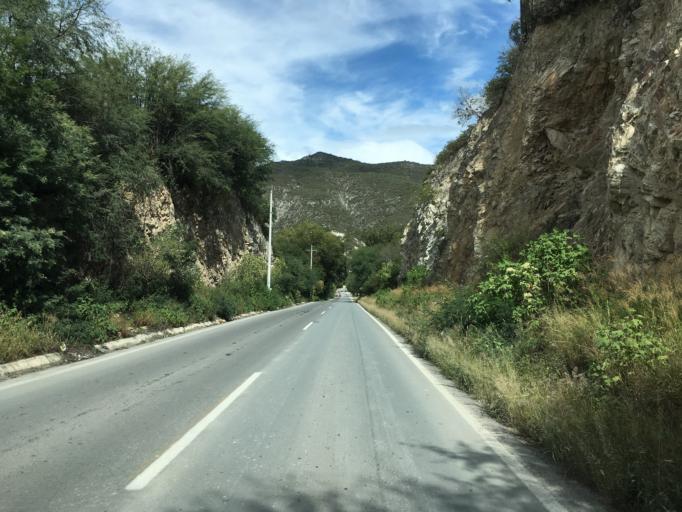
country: MX
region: Hidalgo
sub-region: San Agustin Metzquititlan
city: Mezquititlan
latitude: 20.4959
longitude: -98.6956
